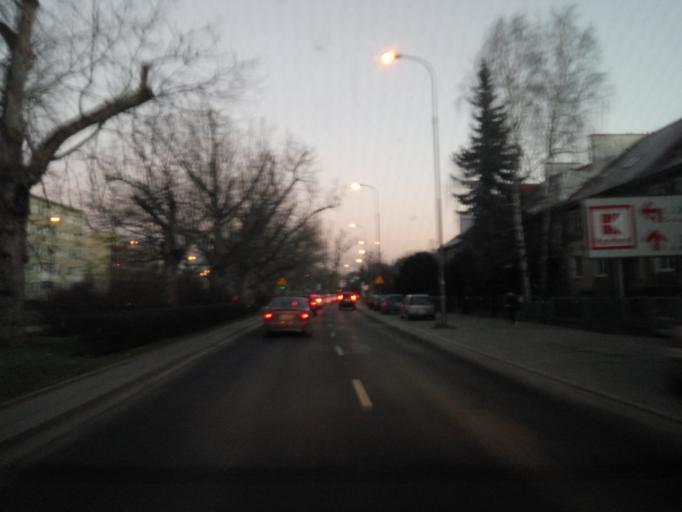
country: PL
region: Lower Silesian Voivodeship
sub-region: Powiat wroclawski
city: Wroclaw
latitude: 51.0861
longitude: 17.0130
